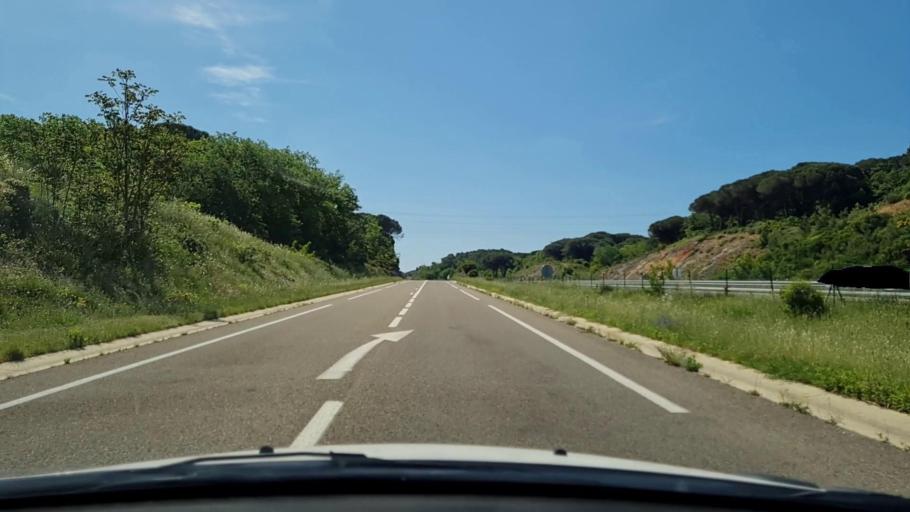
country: FR
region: Languedoc-Roussillon
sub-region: Departement du Gard
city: La Calmette
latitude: 43.9163
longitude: 4.2632
